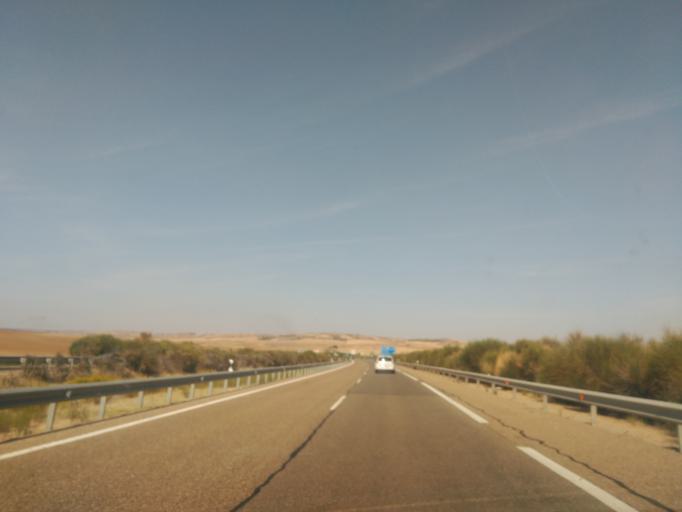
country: ES
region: Castille and Leon
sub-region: Provincia de Zamora
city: Castrillo de la Guarena
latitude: 41.2146
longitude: -5.3212
